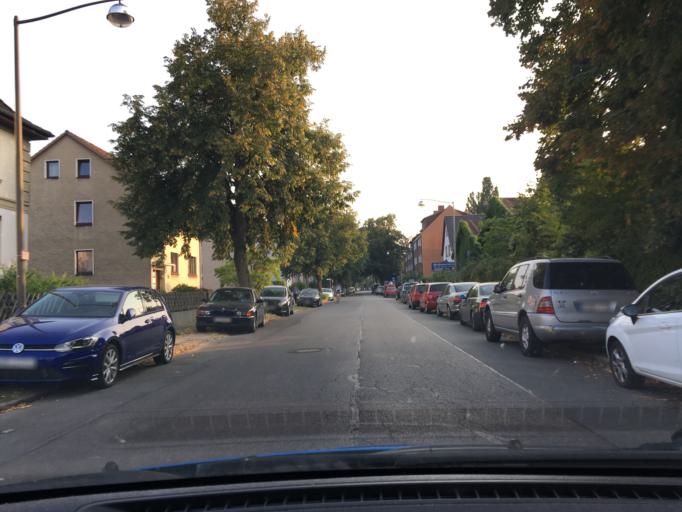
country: DE
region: Lower Saxony
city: Langenhagen
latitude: 52.4523
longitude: 9.7387
